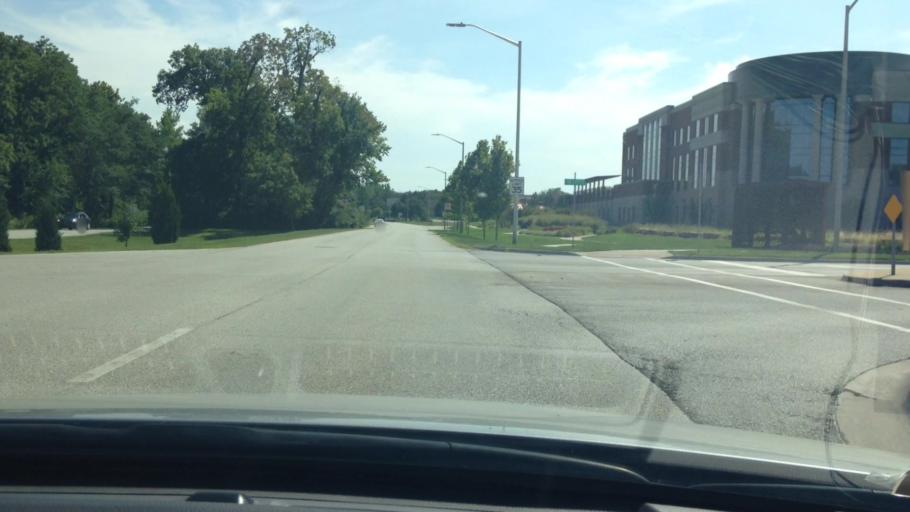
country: US
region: Kansas
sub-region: Johnson County
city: Leawood
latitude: 38.9167
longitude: -94.6341
